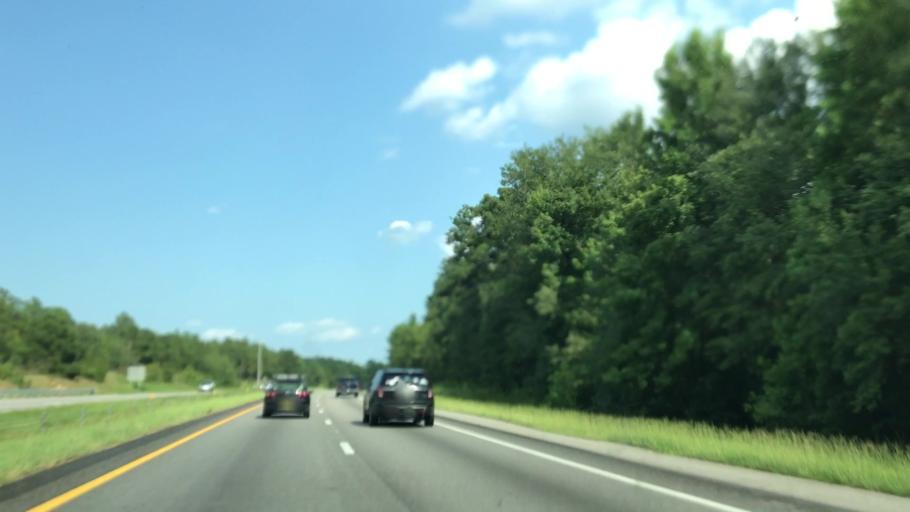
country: US
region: South Carolina
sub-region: Calhoun County
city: Oak Grove
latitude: 33.7635
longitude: -80.9603
